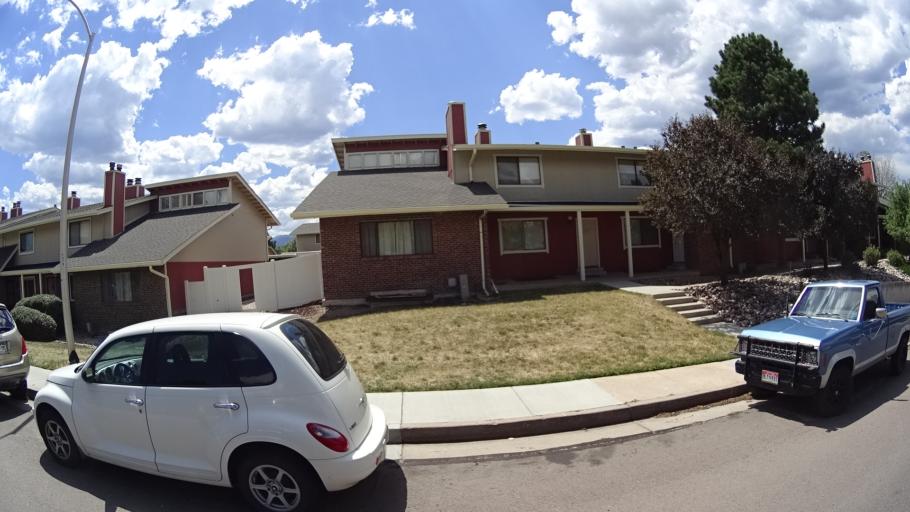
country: US
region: Colorado
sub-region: El Paso County
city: Air Force Academy
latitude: 38.9300
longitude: -104.8316
